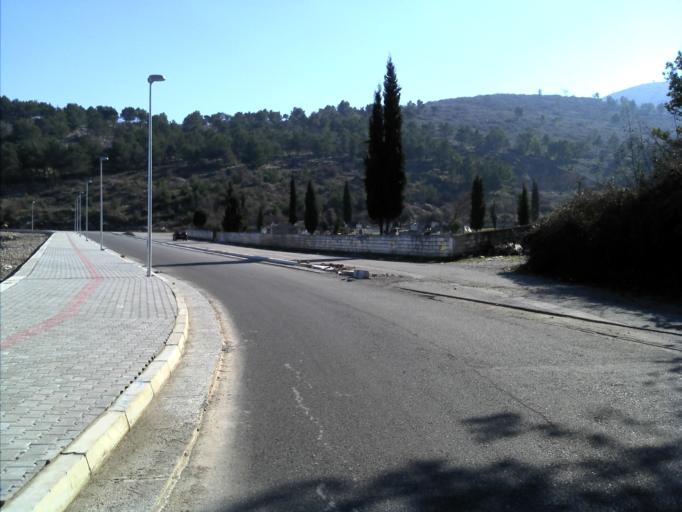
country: AL
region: Shkoder
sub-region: Rrethi i Shkodres
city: Berdica e Madhe
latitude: 42.0562
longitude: 19.4672
